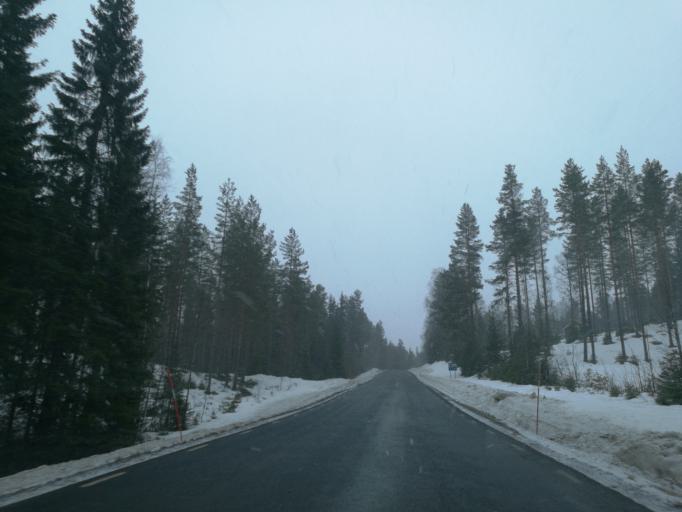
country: SE
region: Vaermland
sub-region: Torsby Kommun
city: Torsby
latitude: 60.6661
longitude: 12.6989
